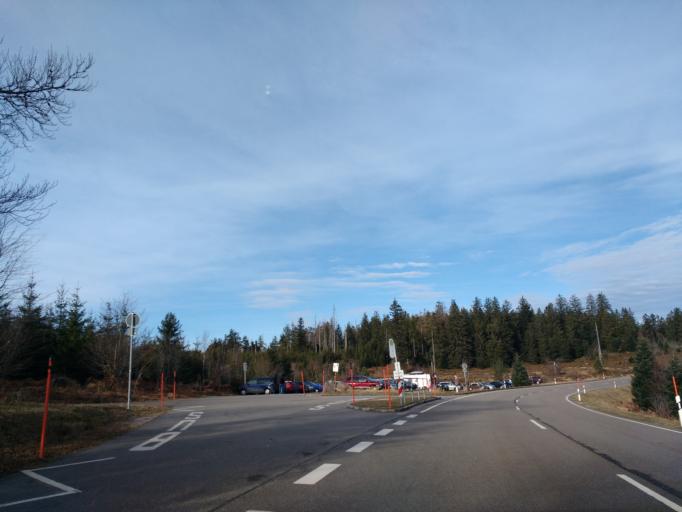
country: DE
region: Baden-Wuerttemberg
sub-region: Freiburg Region
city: Oppenau
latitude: 48.5059
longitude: 8.2238
